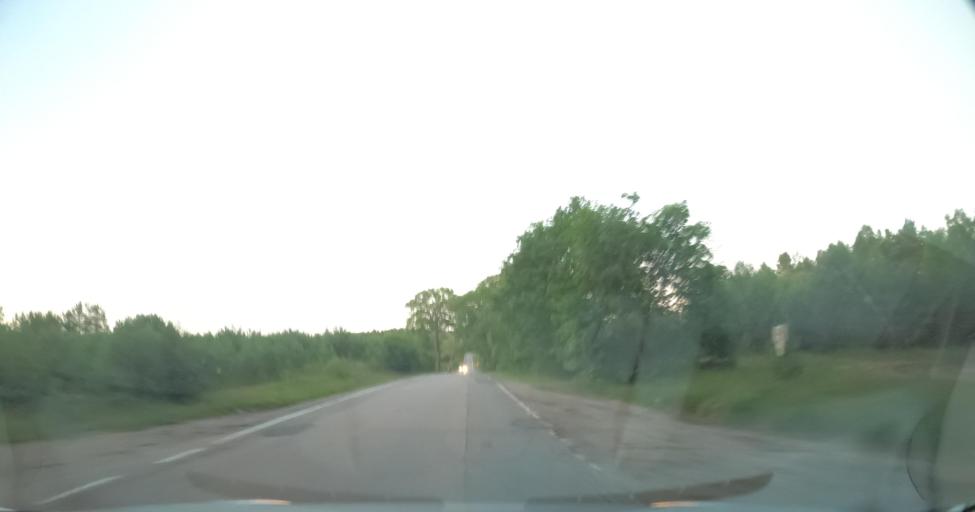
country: PL
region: Pomeranian Voivodeship
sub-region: Powiat wejherowski
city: Luzino
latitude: 54.4649
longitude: 18.1200
